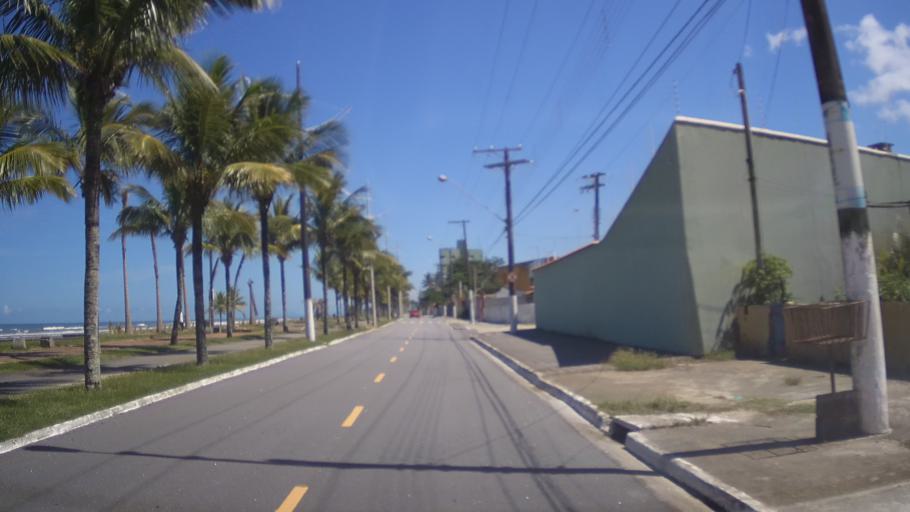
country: BR
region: Sao Paulo
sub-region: Mongagua
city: Mongagua
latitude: -24.0813
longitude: -46.5902
